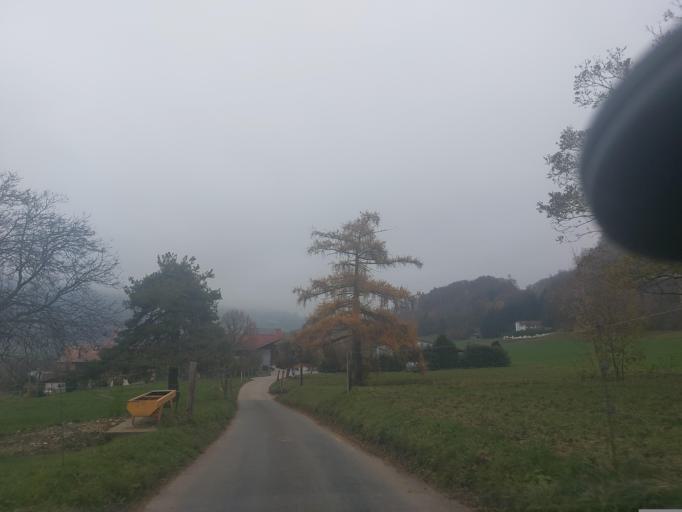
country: CH
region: Vaud
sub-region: Riviera-Pays-d'Enhaut District
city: Blonay
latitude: 46.4827
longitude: 6.8830
